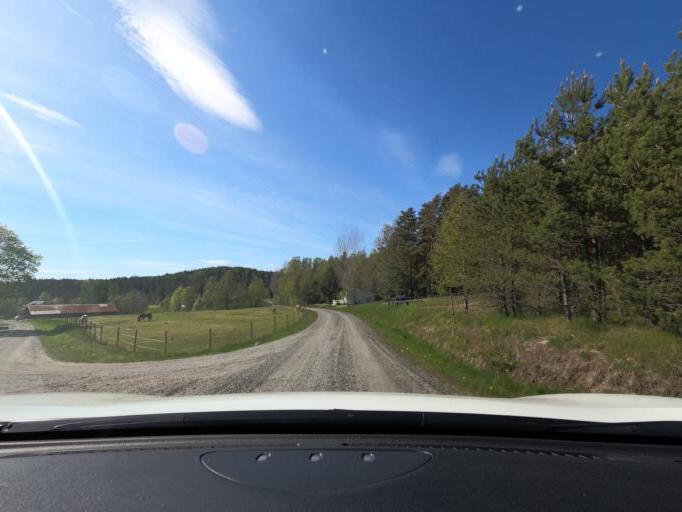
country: SE
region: Vaestra Goetaland
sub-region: Harryda Kommun
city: Ravlanda
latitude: 57.5866
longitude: 12.4928
